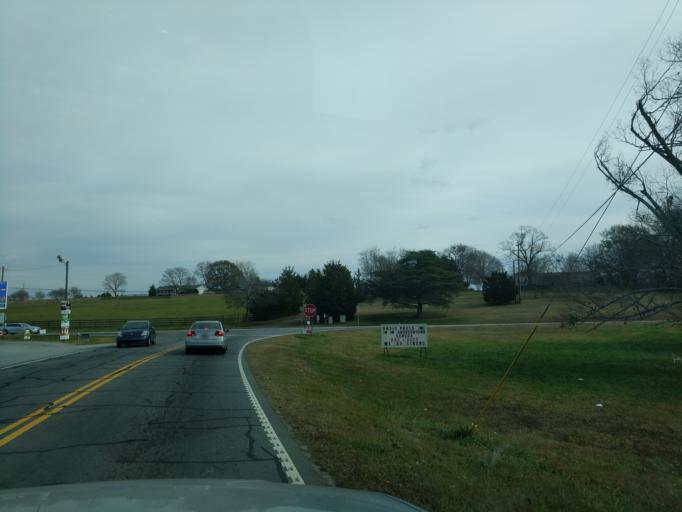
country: US
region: South Carolina
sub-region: Pickens County
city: Central
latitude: 34.6949
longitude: -82.7469
